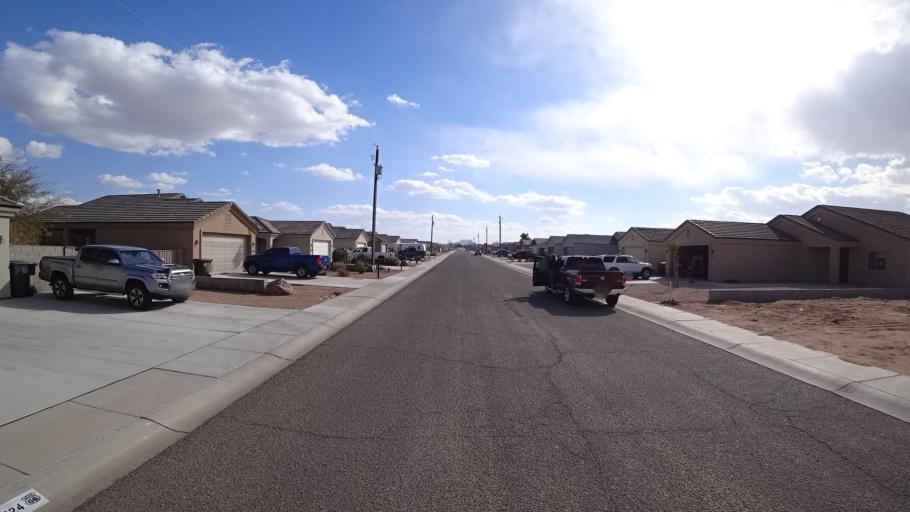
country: US
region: Arizona
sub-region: Mohave County
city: New Kingman-Butler
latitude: 35.2314
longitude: -114.0233
